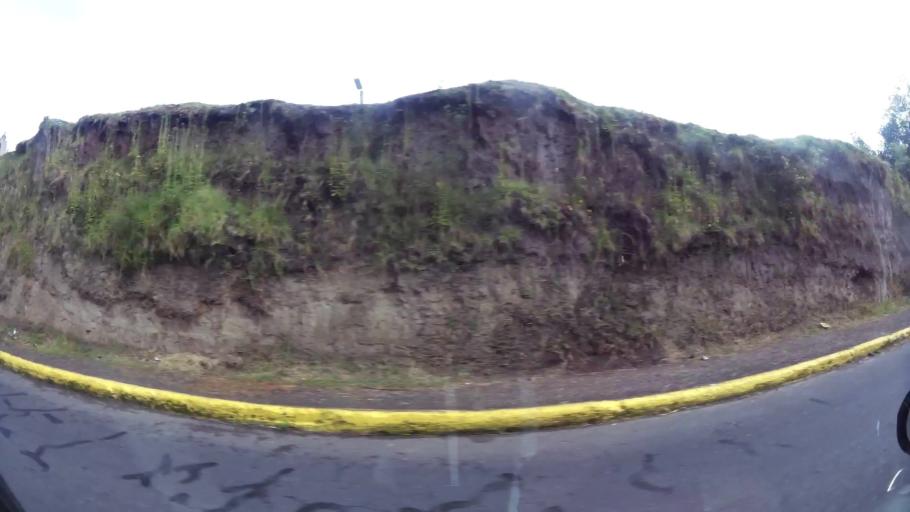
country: EC
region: Pichincha
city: Quito
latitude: -0.2366
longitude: -78.4835
